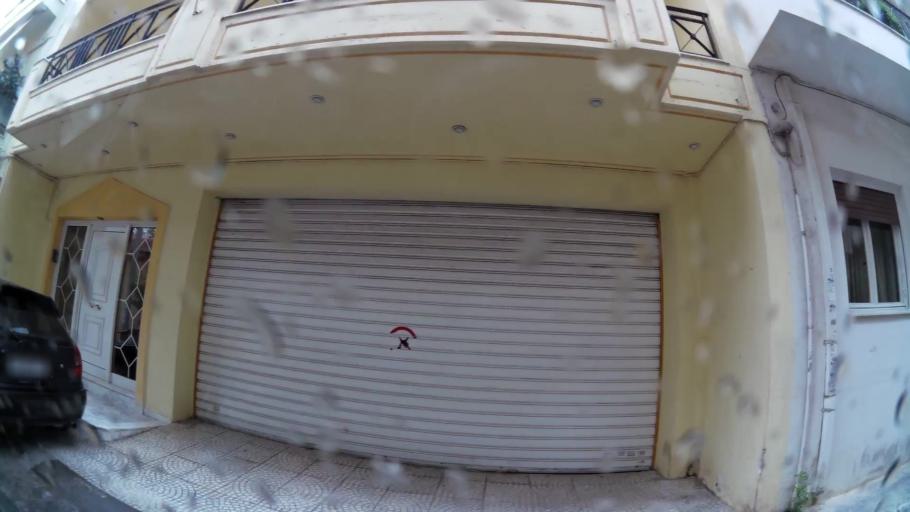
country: GR
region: Attica
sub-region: Nomos Piraios
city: Nikaia
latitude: 37.9601
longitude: 23.6533
